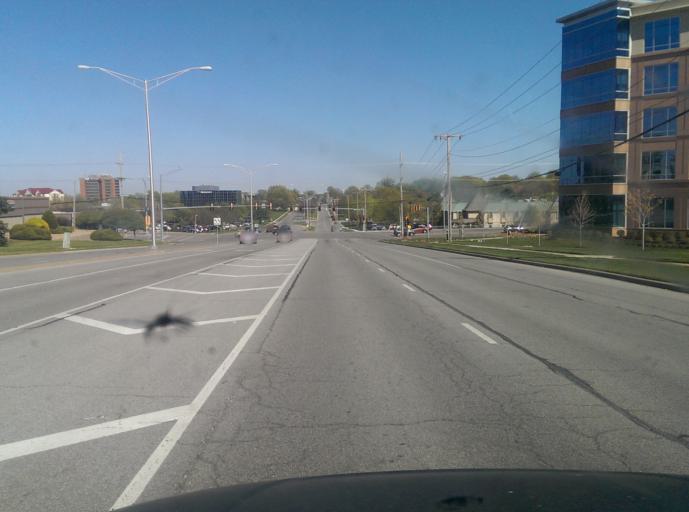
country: US
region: Kansas
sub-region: Johnson County
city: Leawood
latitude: 38.9275
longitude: -94.6507
